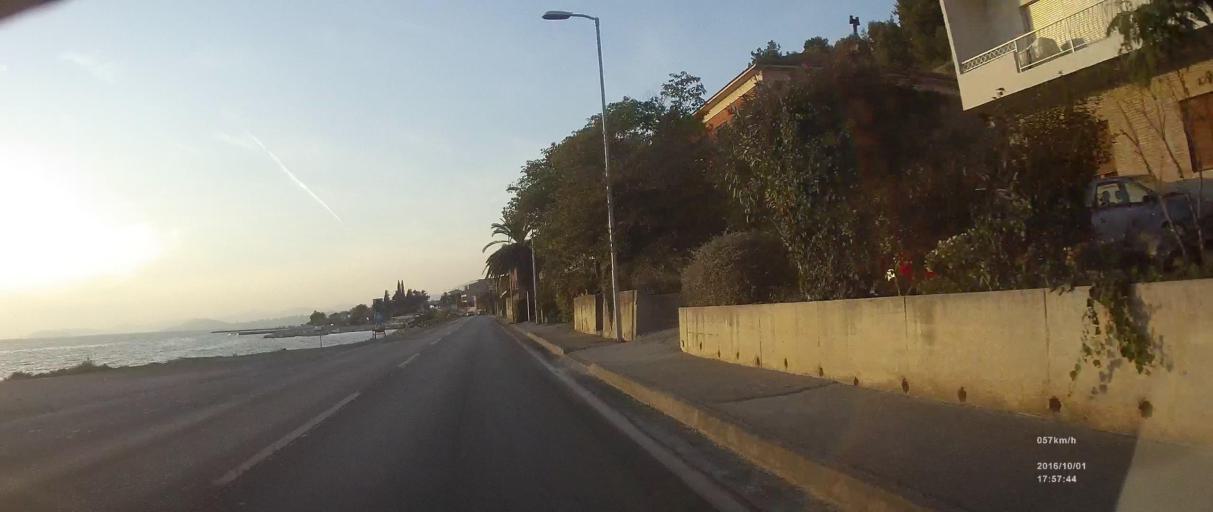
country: HR
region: Splitsko-Dalmatinska
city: Podstrana
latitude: 43.4718
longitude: 16.5723
